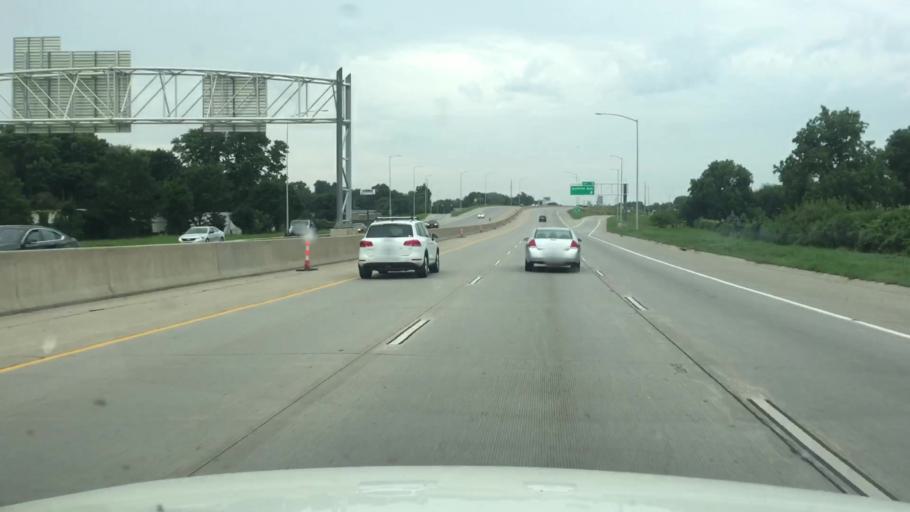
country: US
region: Iowa
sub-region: Polk County
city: Des Moines
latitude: 41.6202
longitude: -93.5765
